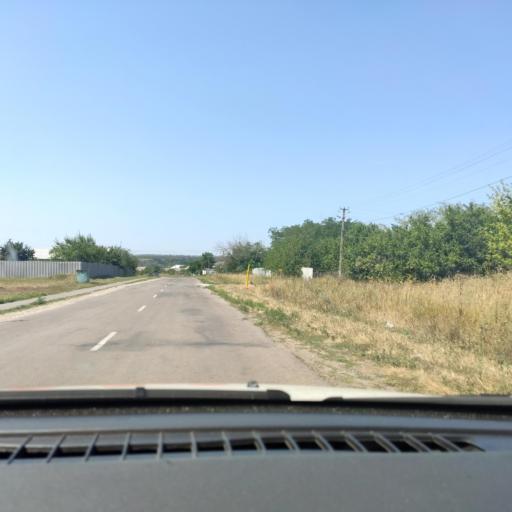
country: RU
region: Voronezj
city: Imeni Pervogo Maya
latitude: 50.7185
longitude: 39.3795
